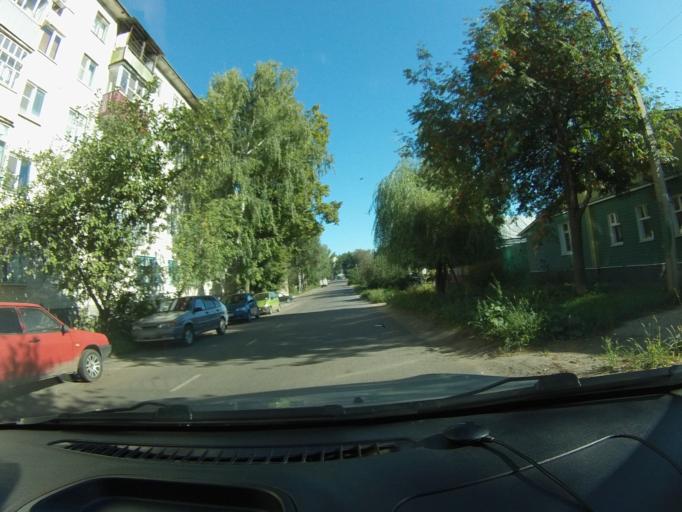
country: RU
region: Tambov
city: Tambov
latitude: 52.7558
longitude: 41.4253
